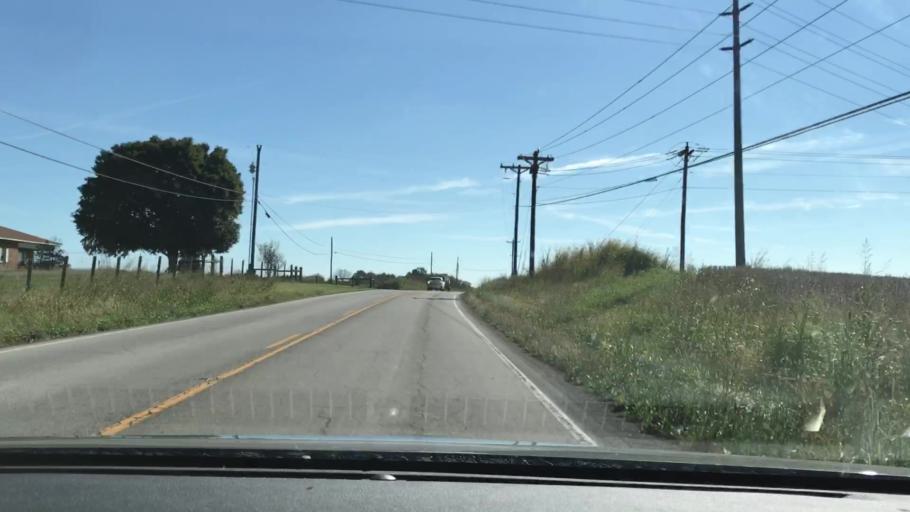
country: US
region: Kentucky
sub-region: Christian County
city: Hopkinsville
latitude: 36.8605
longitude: -87.4343
